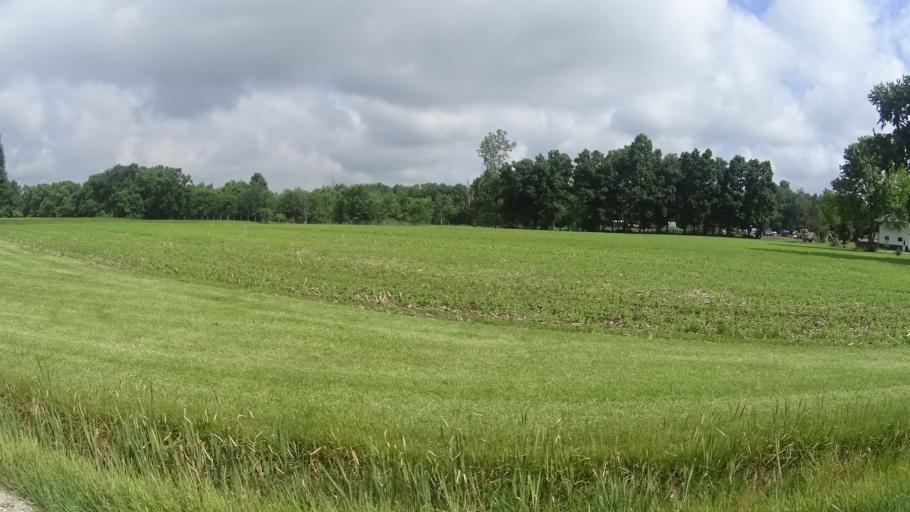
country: US
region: Ohio
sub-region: Huron County
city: Wakeman
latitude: 41.3194
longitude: -82.4259
